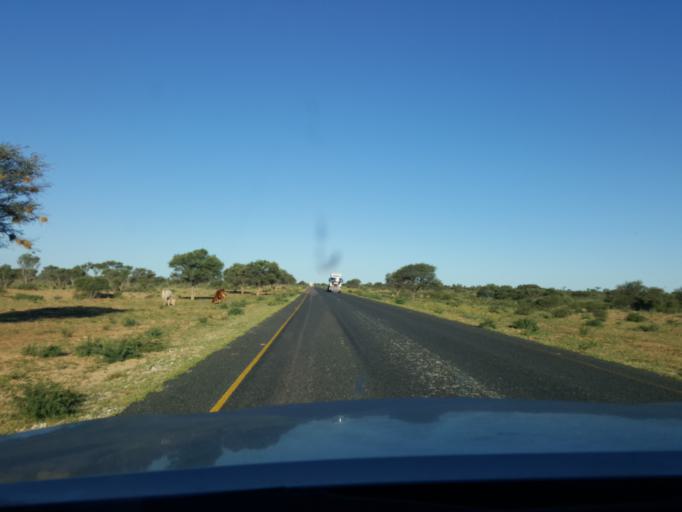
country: BW
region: Southern
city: Khakhea
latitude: -24.2566
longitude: 23.3046
